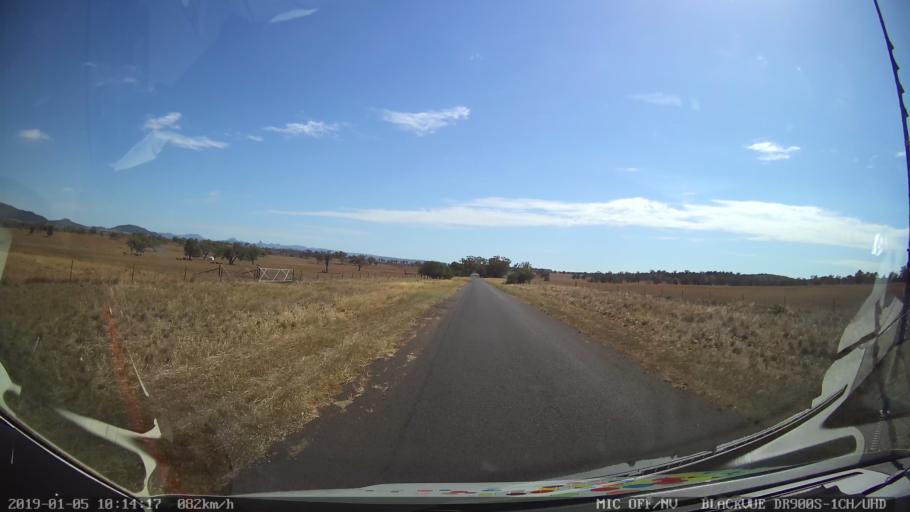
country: AU
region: New South Wales
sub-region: Gilgandra
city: Gilgandra
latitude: -31.5943
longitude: 148.9329
